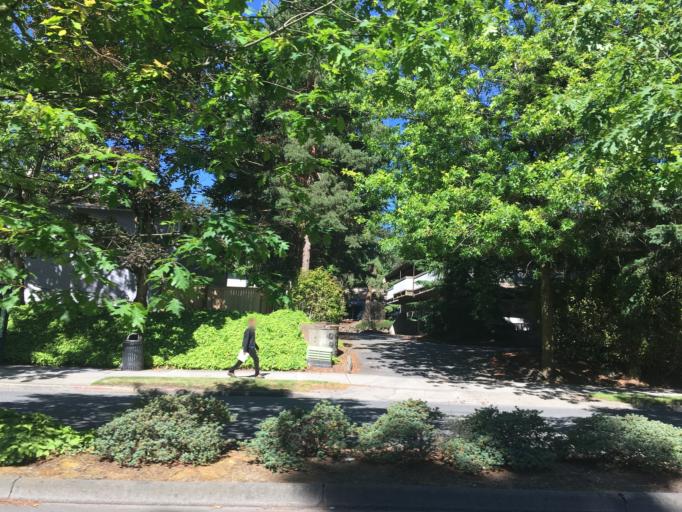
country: US
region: Washington
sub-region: King County
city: Redmond
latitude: 47.6454
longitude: -122.1429
